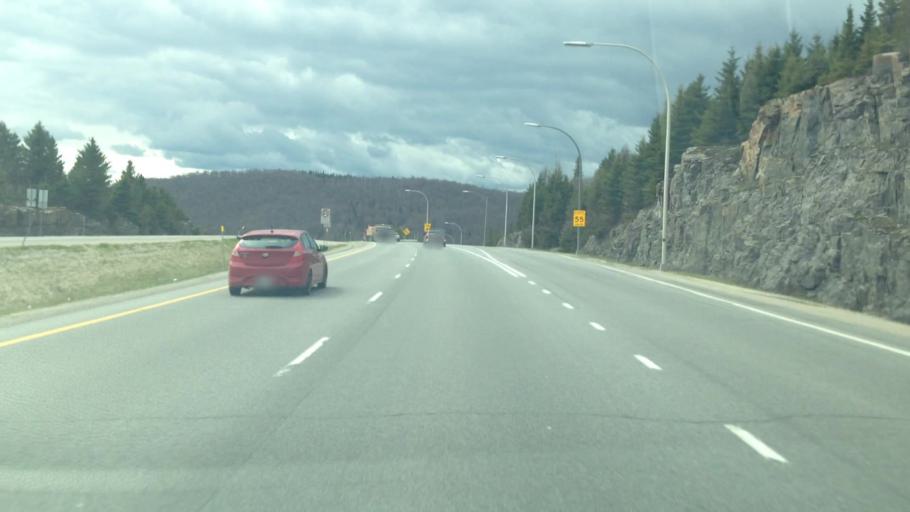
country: CA
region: Quebec
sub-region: Laurentides
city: Val-David
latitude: 45.9894
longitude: -74.1904
